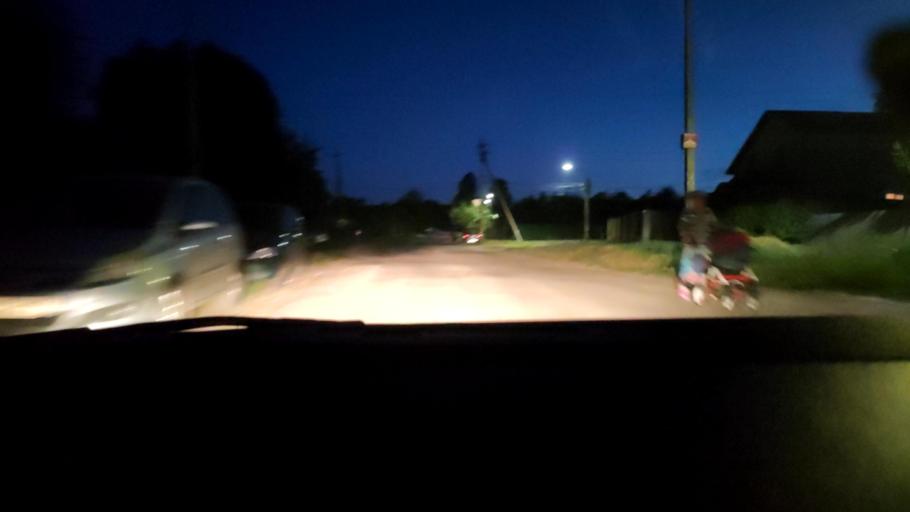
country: RU
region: Voronezj
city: Semiluki
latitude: 51.6895
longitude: 39.0248
